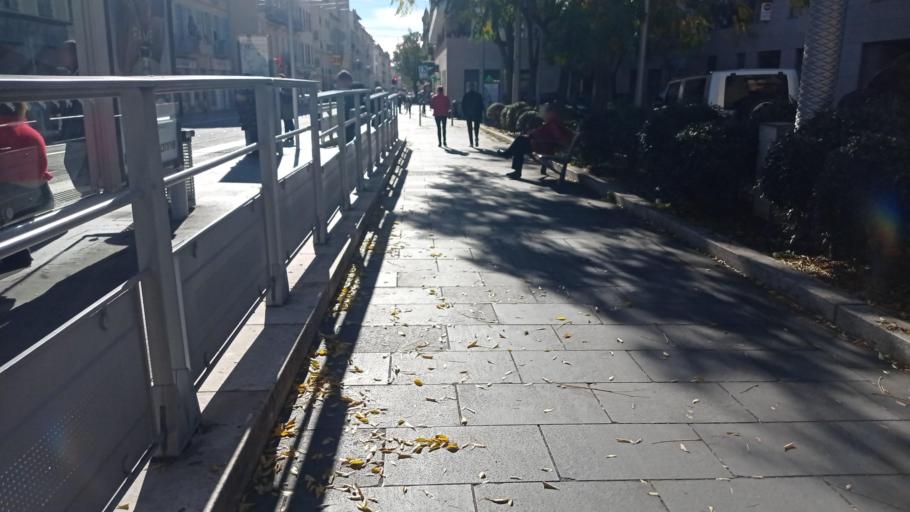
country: FR
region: Provence-Alpes-Cote d'Azur
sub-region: Departement des Alpes-Maritimes
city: Nice
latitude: 43.7155
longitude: 7.2614
